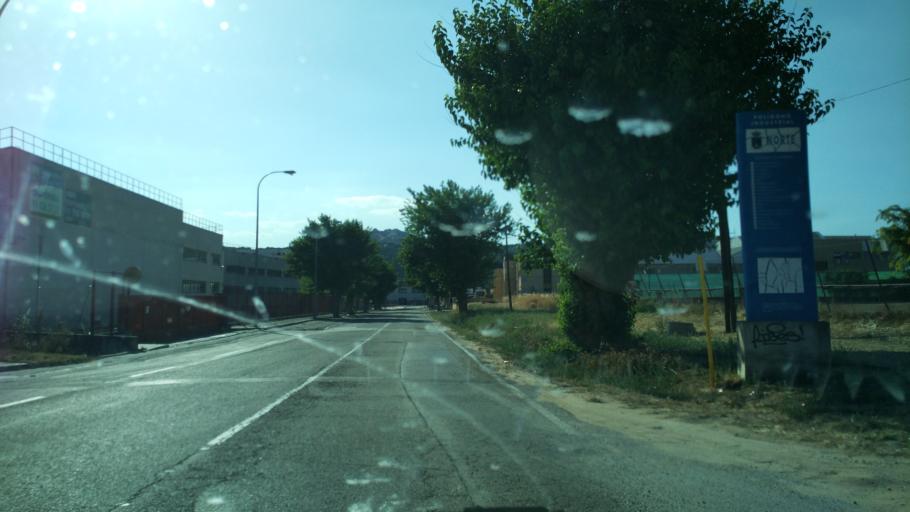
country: ES
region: Madrid
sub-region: Provincia de Madrid
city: San Agustin de Guadalix
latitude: 40.6906
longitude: -3.6060
